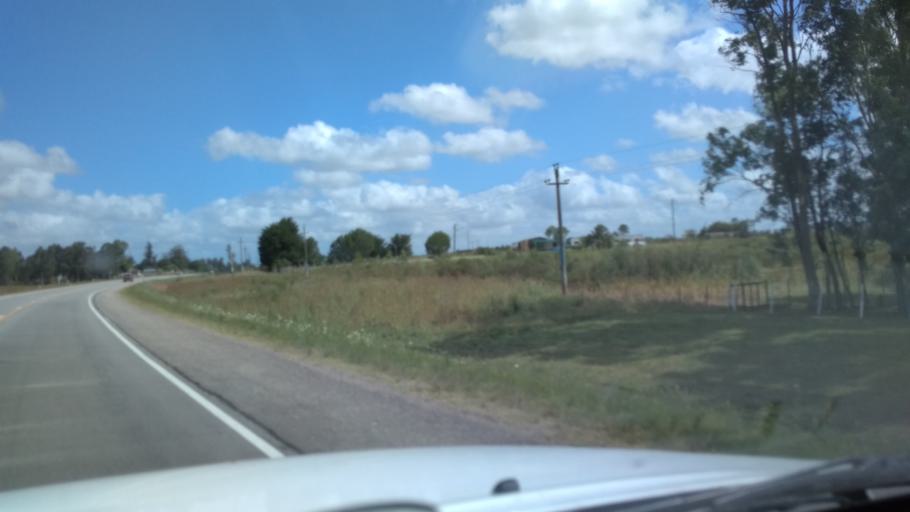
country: UY
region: Canelones
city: Sauce
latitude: -34.6070
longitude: -56.0485
